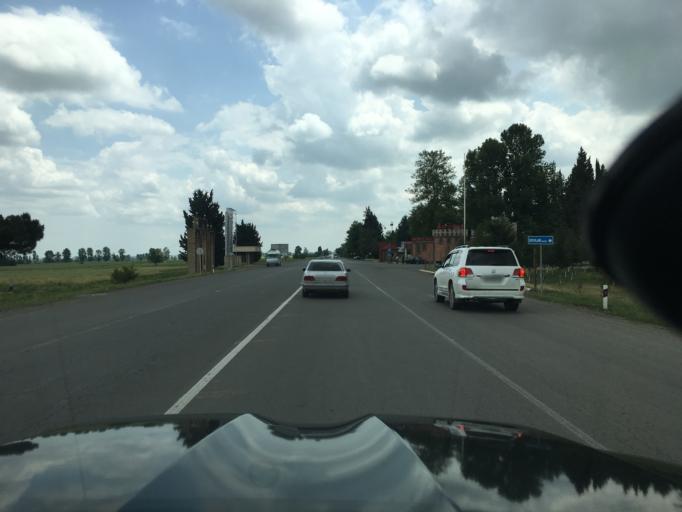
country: AZ
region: Tovuz
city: Tovuz
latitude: 40.9597
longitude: 45.7237
